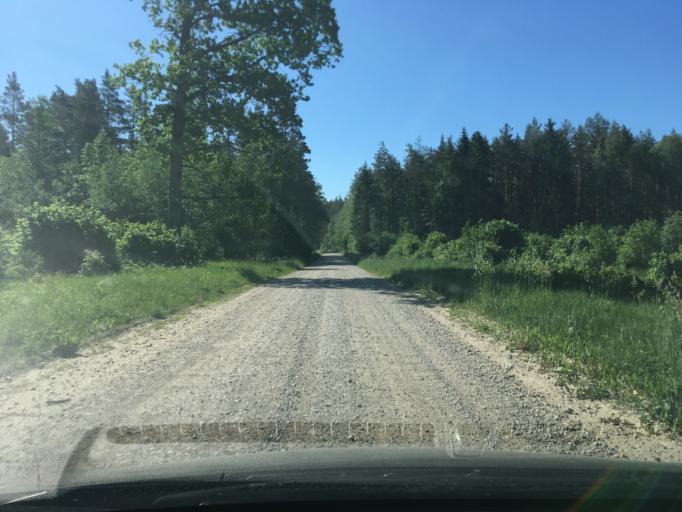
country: EE
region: Laeaene
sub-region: Lihula vald
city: Lihula
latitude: 58.6408
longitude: 23.7900
